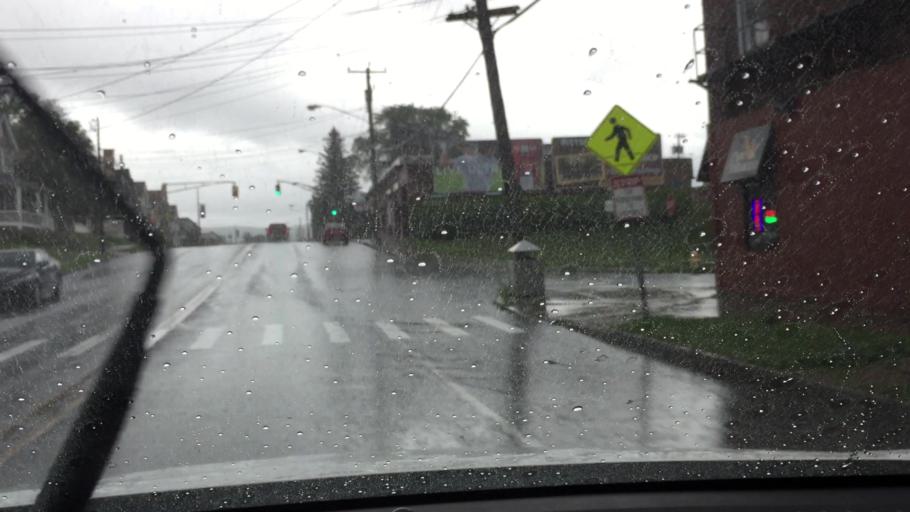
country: US
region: Massachusetts
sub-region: Berkshire County
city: Pittsfield
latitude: 42.4573
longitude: -73.2403
